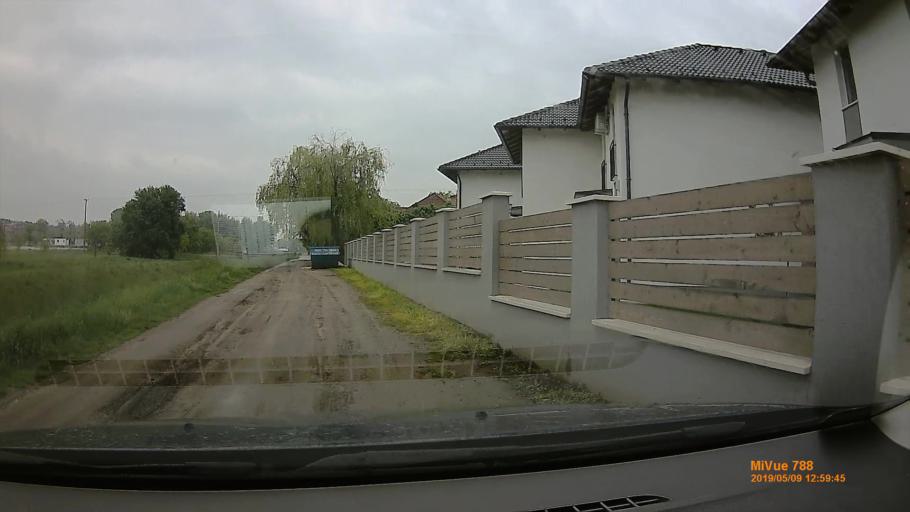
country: HU
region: Budapest
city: Budapest XVI. keruelet
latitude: 47.5366
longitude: 19.1746
